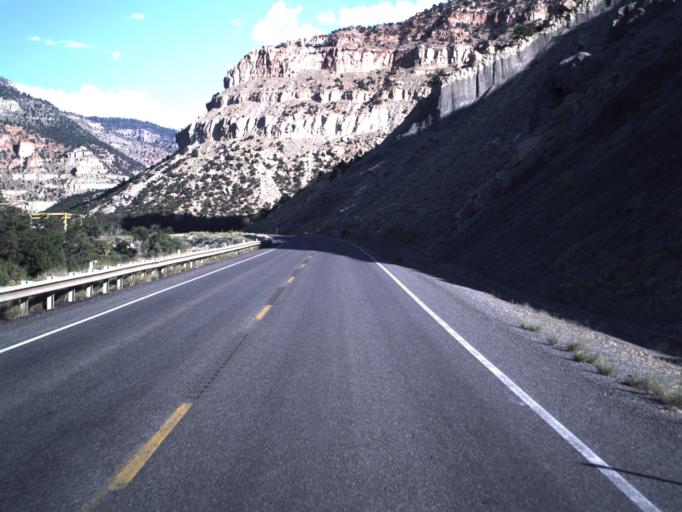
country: US
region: Utah
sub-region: Emery County
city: Huntington
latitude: 39.3899
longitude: -111.0892
